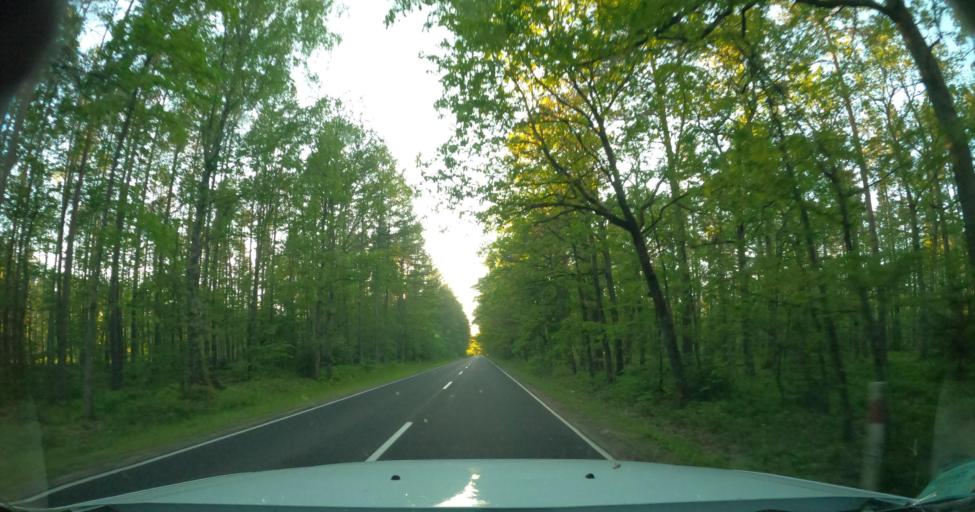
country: PL
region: Pomeranian Voivodeship
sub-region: Powiat slupski
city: Potegowo
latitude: 54.4049
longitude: 17.4503
